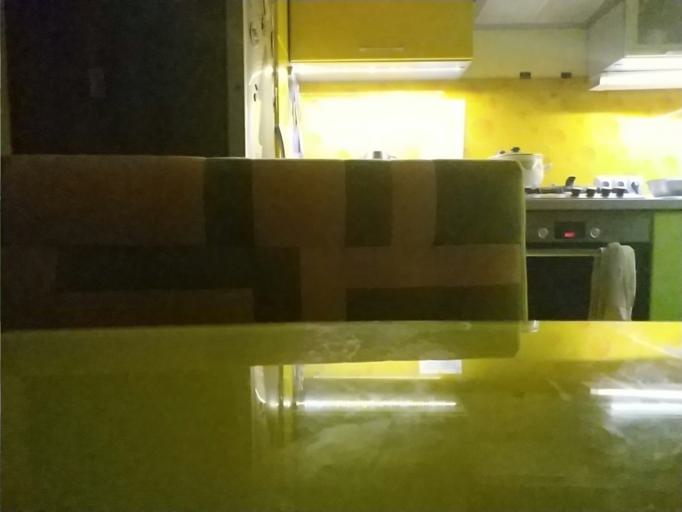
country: RU
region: Republic of Karelia
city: Pyaozerskiy
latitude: 65.5521
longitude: 30.5863
